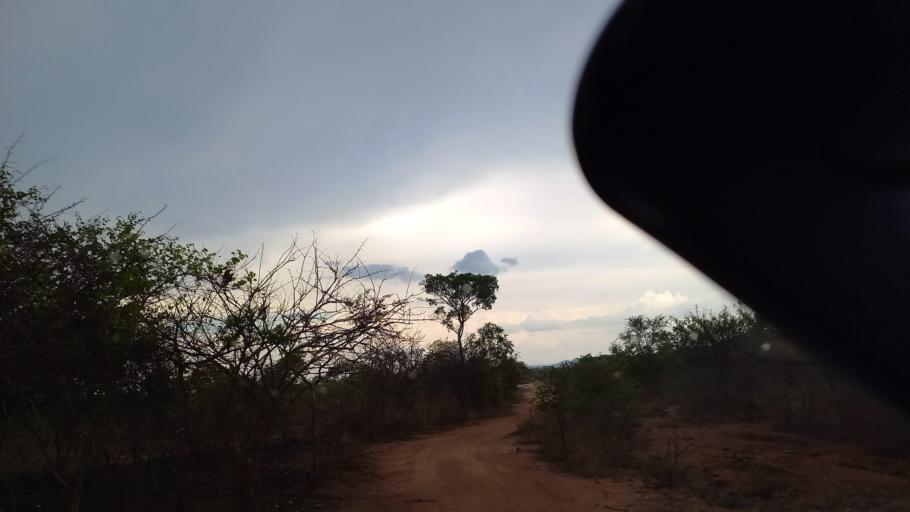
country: ZM
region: Lusaka
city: Kafue
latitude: -15.9939
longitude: 28.2739
